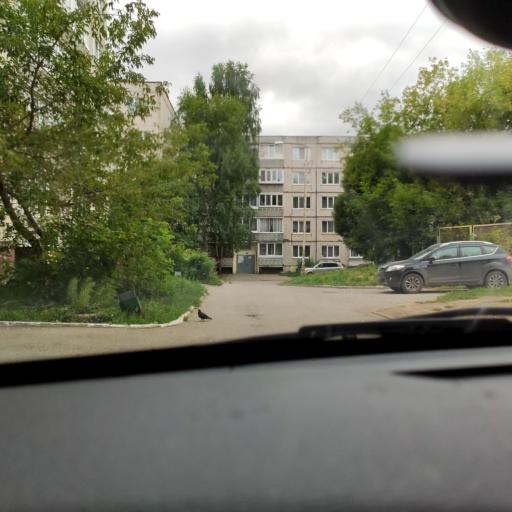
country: RU
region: Perm
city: Dobryanka
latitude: 58.4618
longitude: 56.3965
